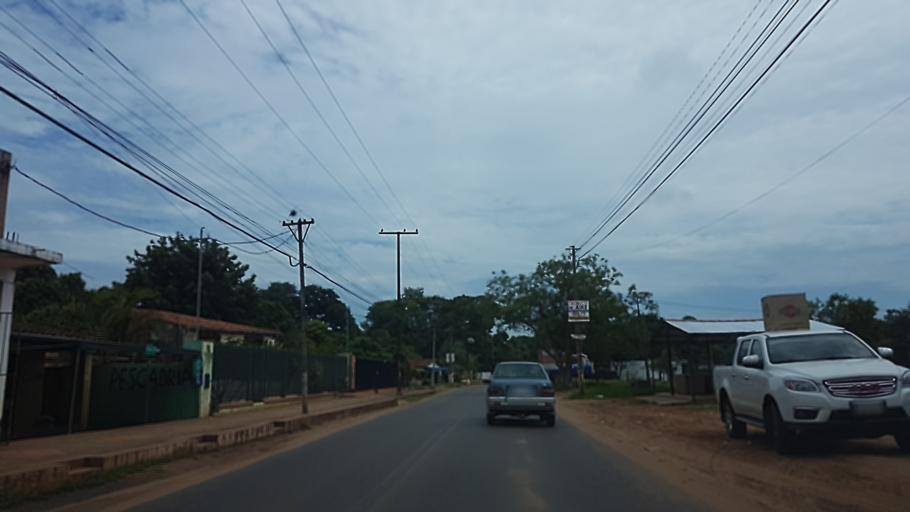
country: PY
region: Central
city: Capiata
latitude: -25.3429
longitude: -57.4609
